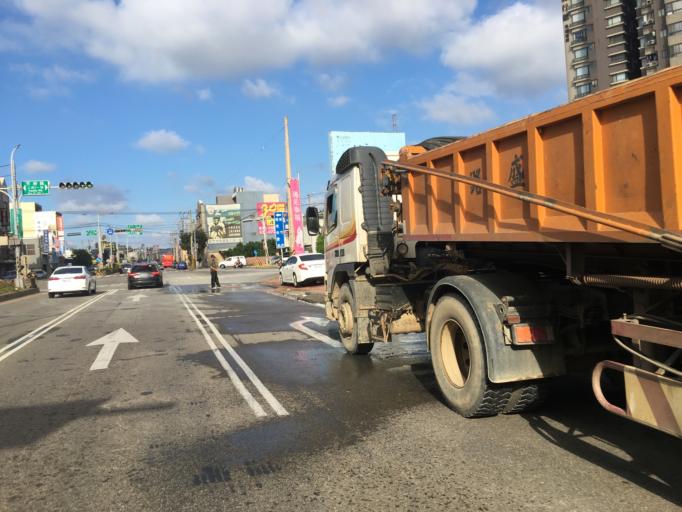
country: TW
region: Taiwan
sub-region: Hsinchu
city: Hsinchu
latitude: 24.8390
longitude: 120.9311
